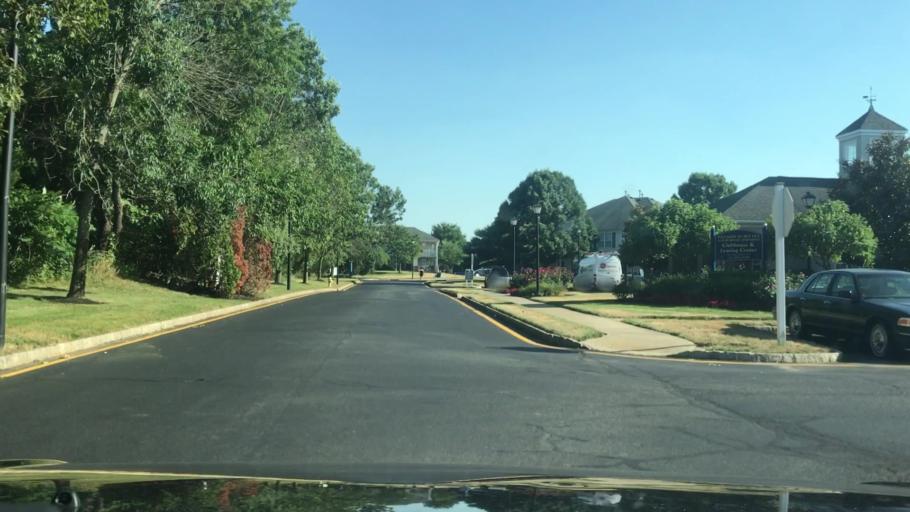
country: US
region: New Jersey
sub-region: Ocean County
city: Toms River
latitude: 39.9887
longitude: -74.1973
